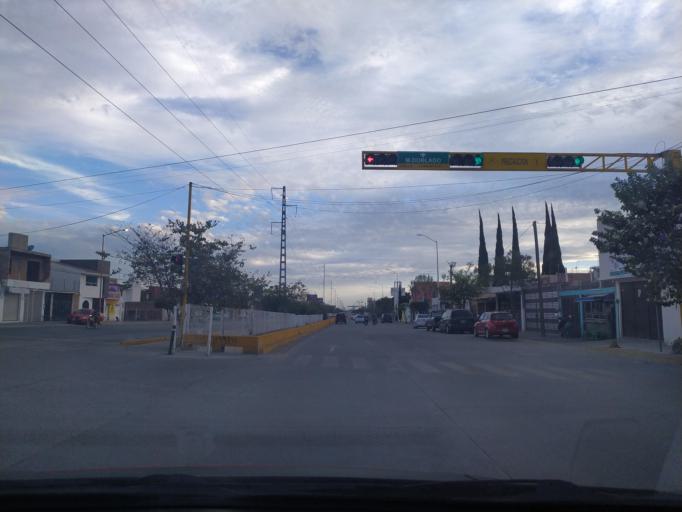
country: LA
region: Oudomxai
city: Muang La
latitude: 21.0275
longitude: 101.8695
